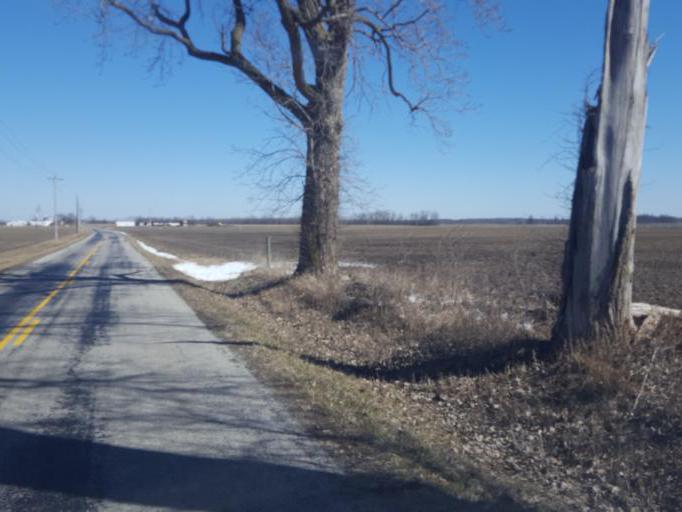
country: US
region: Ohio
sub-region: Wyandot County
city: Upper Sandusky
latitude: 40.6835
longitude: -83.2991
